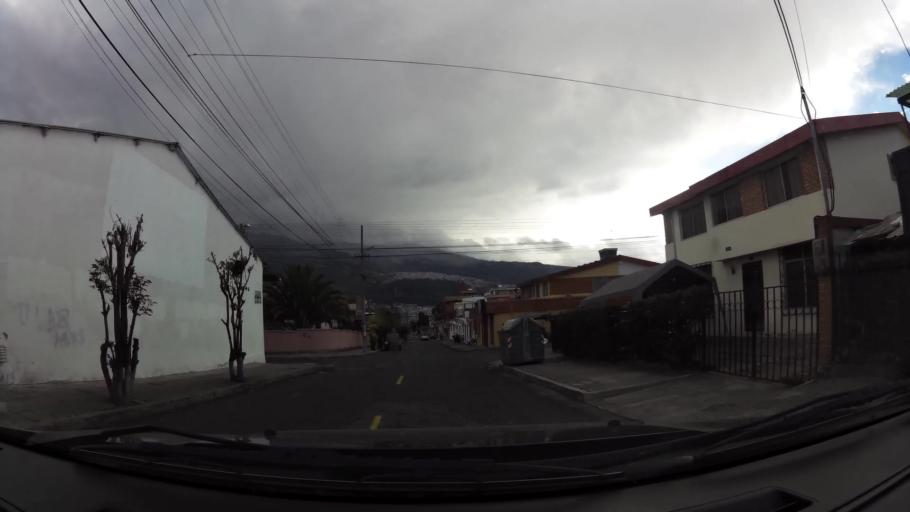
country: EC
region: Pichincha
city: Quito
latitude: -0.1319
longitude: -78.4826
